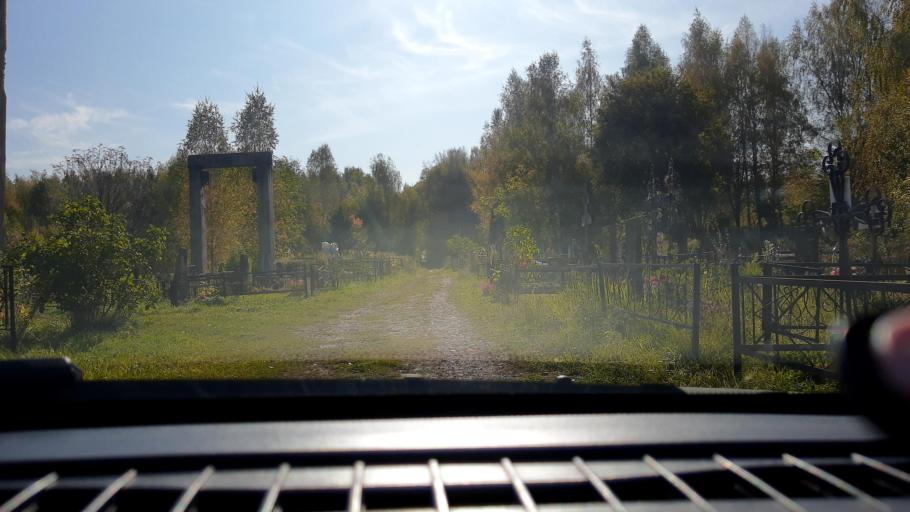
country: RU
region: Nizjnij Novgorod
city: Afonino
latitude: 56.2355
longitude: 44.0621
